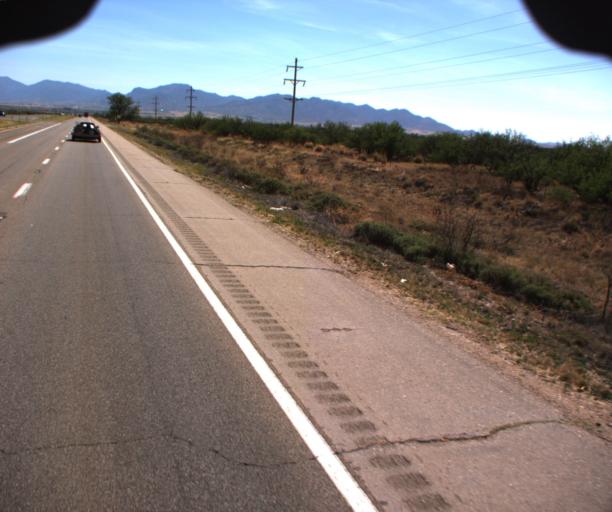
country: US
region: Arizona
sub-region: Cochise County
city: Huachuca City
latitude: 31.6779
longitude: -110.3504
